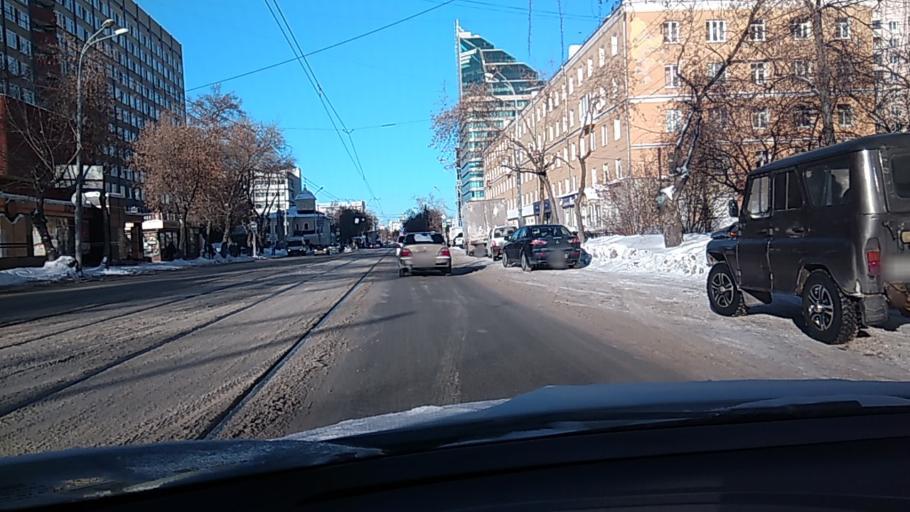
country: RU
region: Sverdlovsk
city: Yekaterinburg
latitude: 56.8212
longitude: 60.6055
